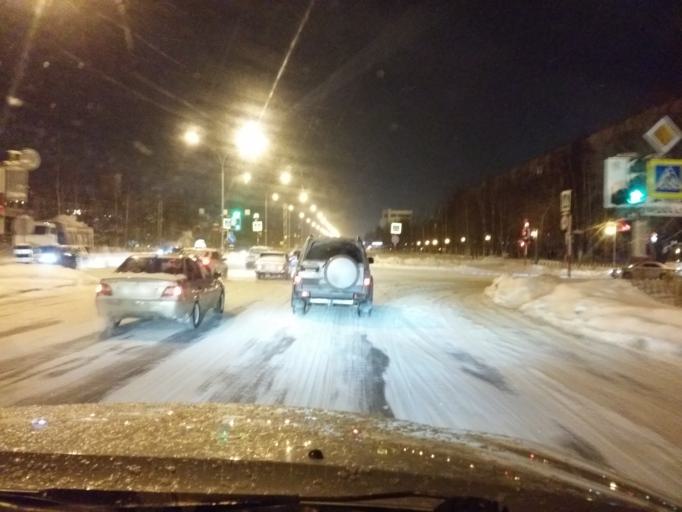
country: RU
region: Khanty-Mansiyskiy Avtonomnyy Okrug
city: Nizhnevartovsk
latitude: 60.9398
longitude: 76.5677
